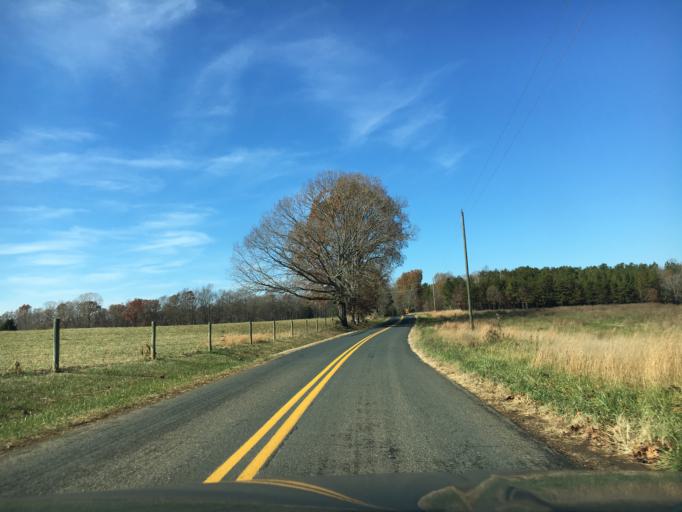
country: US
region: Virginia
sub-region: Buckingham County
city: Buckingham
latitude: 37.4335
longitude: -78.6264
